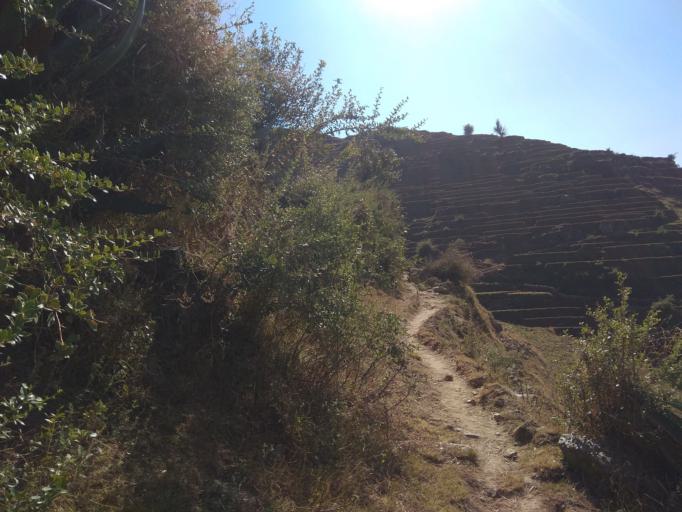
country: NP
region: Far Western
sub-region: Seti Zone
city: Achham
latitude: 29.2469
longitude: 81.6317
